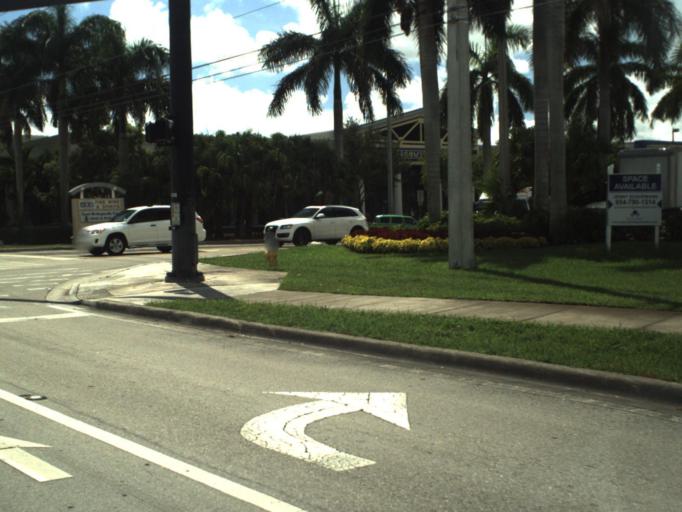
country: US
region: Florida
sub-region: Broward County
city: Cooper City
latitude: 26.0078
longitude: -80.2910
